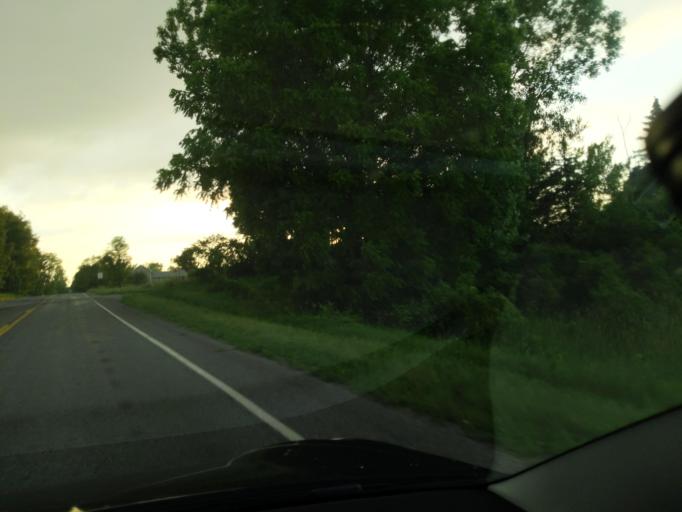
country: US
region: Michigan
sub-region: Ingham County
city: Mason
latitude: 42.5238
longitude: -84.3705
